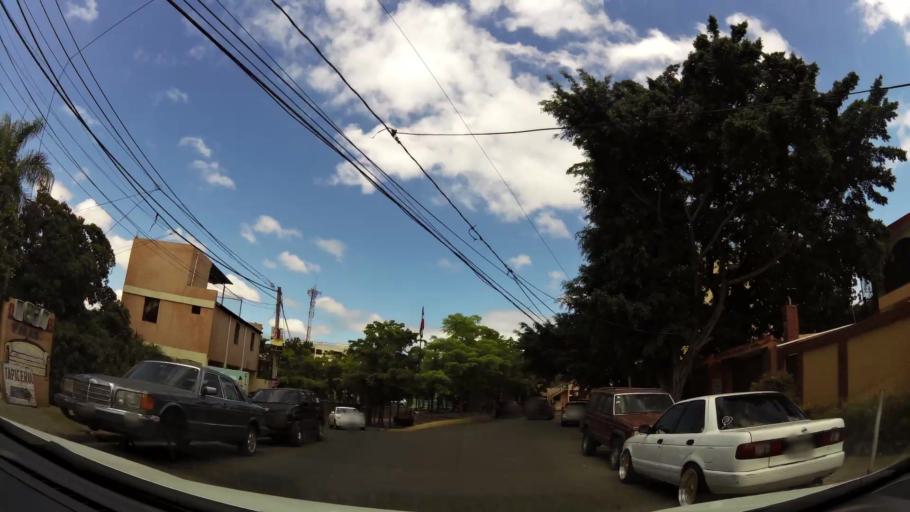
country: DO
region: Nacional
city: Bella Vista
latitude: 18.4680
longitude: -69.9480
